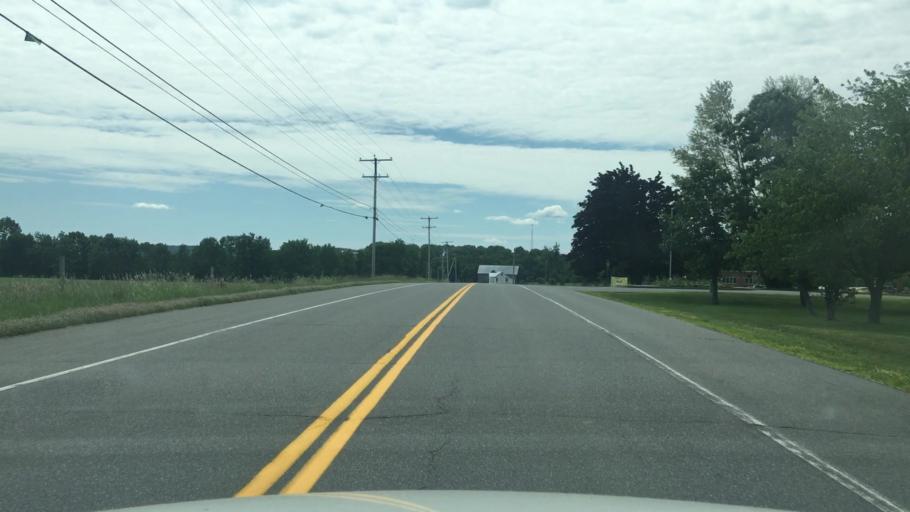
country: US
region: Maine
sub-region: Waldo County
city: Troy
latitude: 44.5531
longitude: -69.2688
